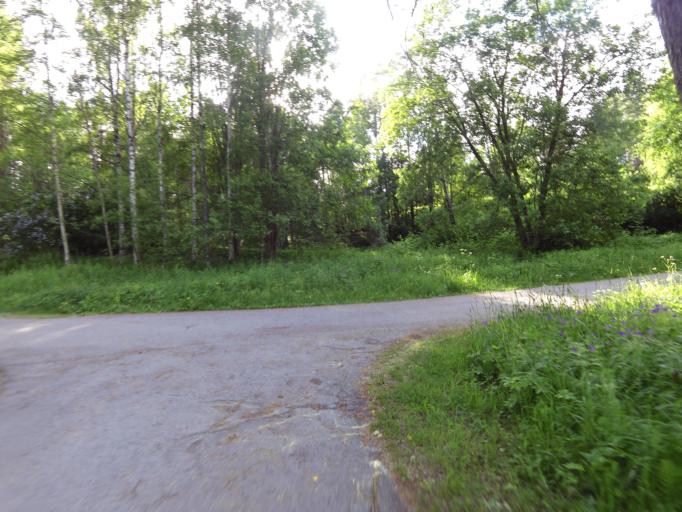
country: SE
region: Gaevleborg
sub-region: Gavle Kommun
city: Gavle
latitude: 60.6877
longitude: 17.1026
